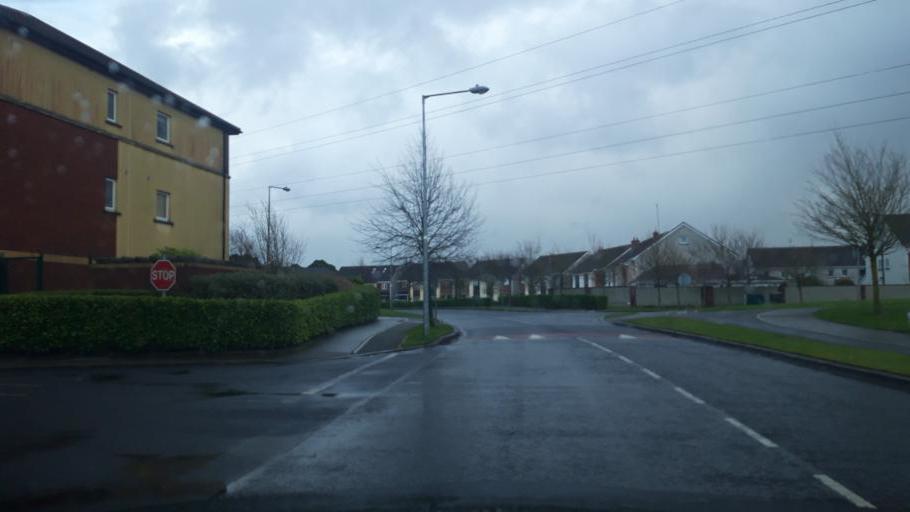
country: IE
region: Leinster
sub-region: Kildare
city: Celbridge
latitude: 53.3319
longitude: -6.5362
